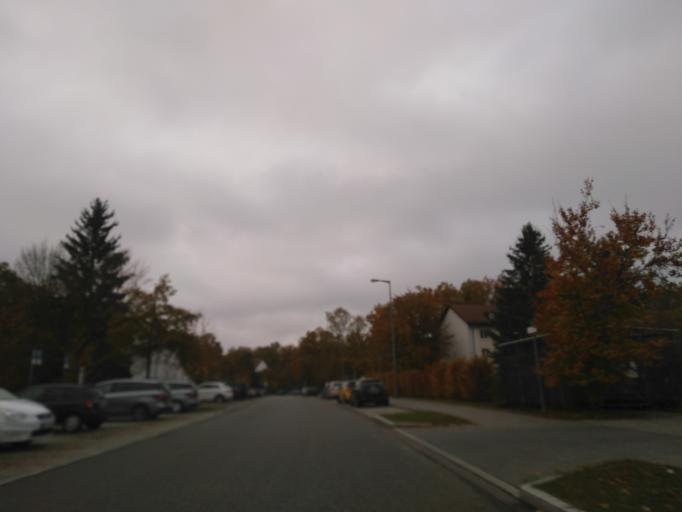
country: DE
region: Bavaria
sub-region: Upper Bavaria
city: Unterhaching
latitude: 48.0898
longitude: 11.5982
